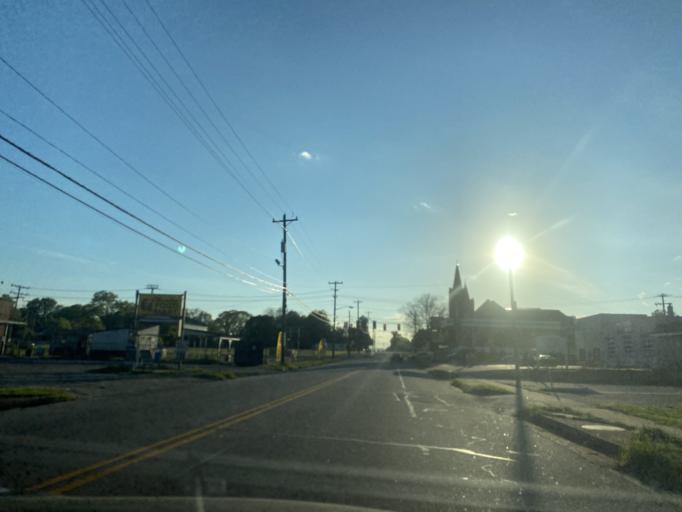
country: US
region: South Carolina
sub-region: Cherokee County
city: East Gaffney
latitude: 35.0795
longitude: -81.6366
